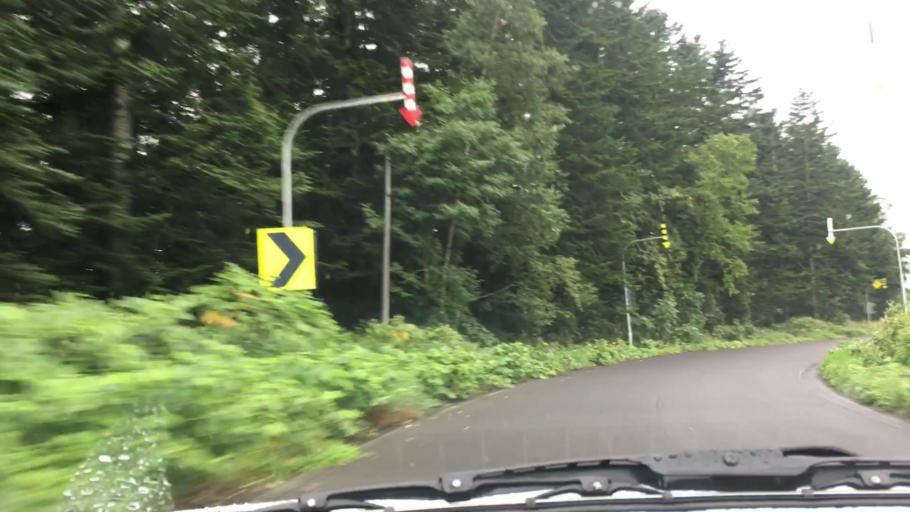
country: JP
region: Hokkaido
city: Niseko Town
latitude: 42.6843
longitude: 140.8212
